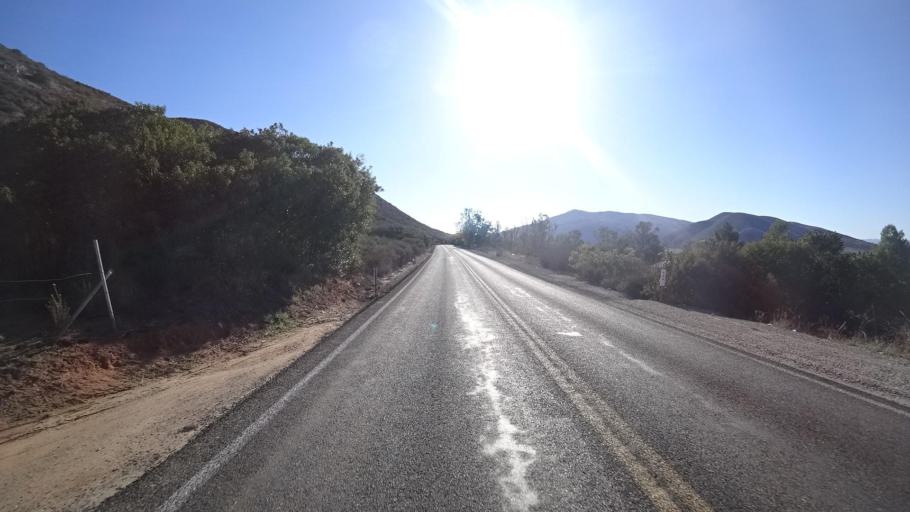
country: MX
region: Baja California
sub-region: Tijuana
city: Villa del Campo
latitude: 32.6213
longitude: -116.7456
